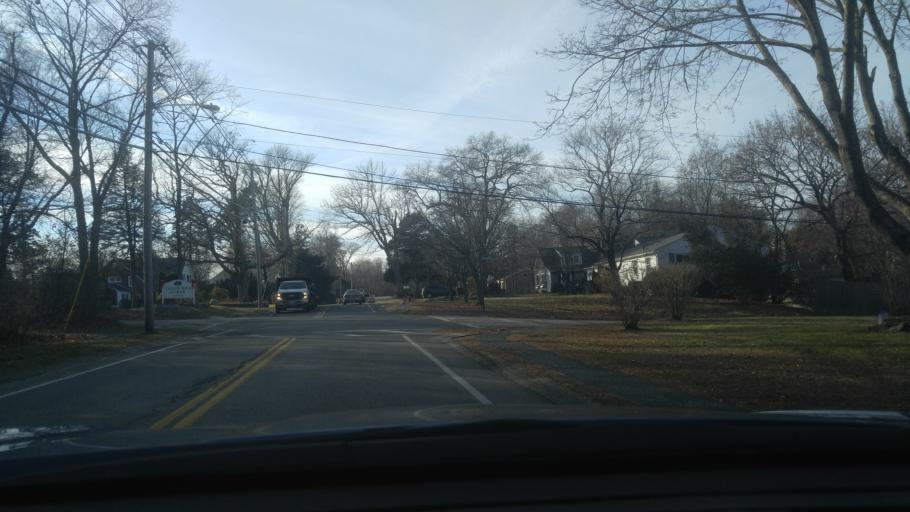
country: US
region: Rhode Island
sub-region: Kent County
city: East Greenwich
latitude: 41.6853
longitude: -71.4648
